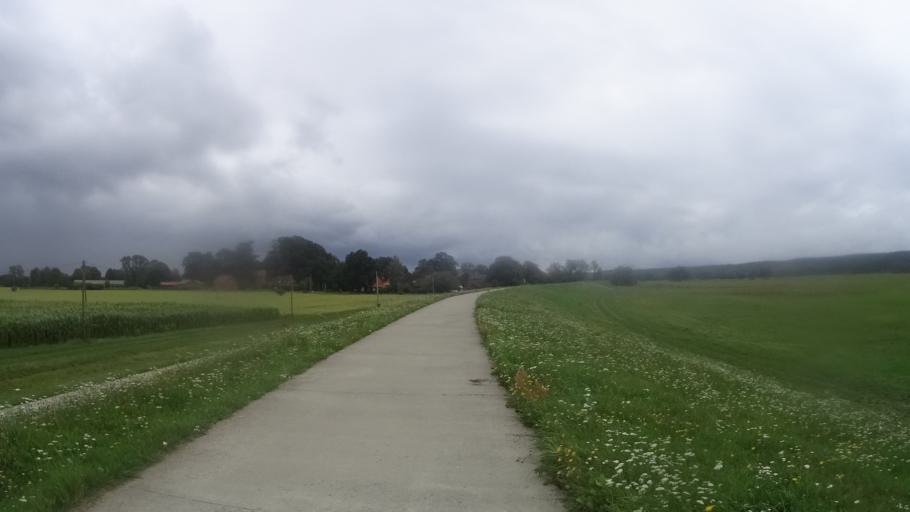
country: DE
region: Lower Saxony
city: Tosterglope
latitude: 53.2760
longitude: 10.8259
